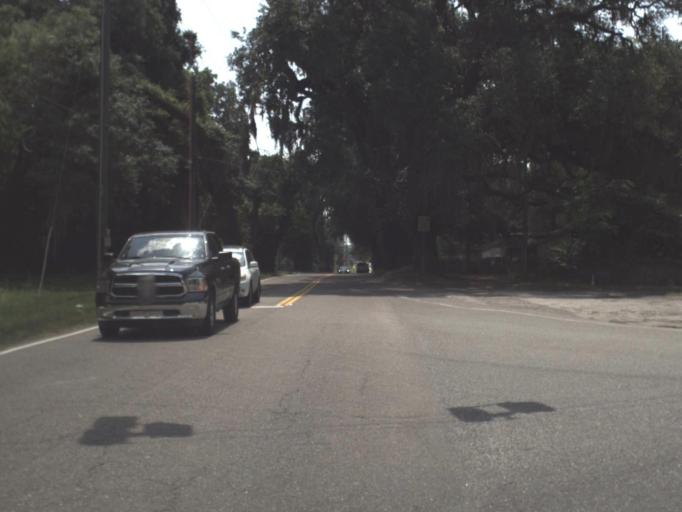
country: US
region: Florida
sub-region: Duval County
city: Jacksonville
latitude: 30.3657
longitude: -81.7417
